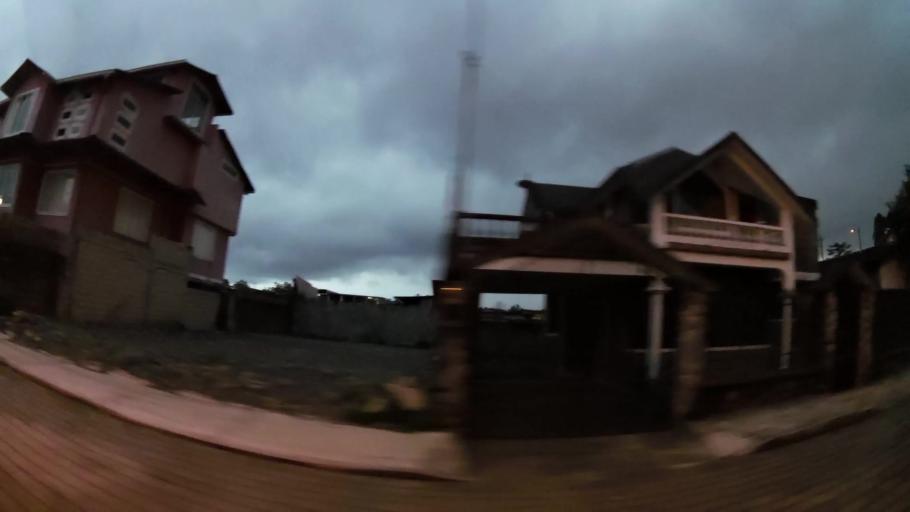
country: EC
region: Pastaza
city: Puyo
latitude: -1.4806
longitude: -78.0046
